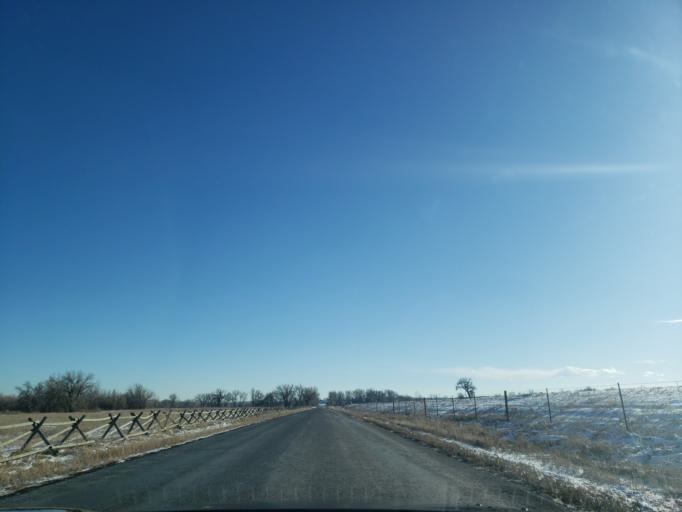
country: US
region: Colorado
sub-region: Larimer County
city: Fort Collins
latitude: 40.5354
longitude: -105.0013
